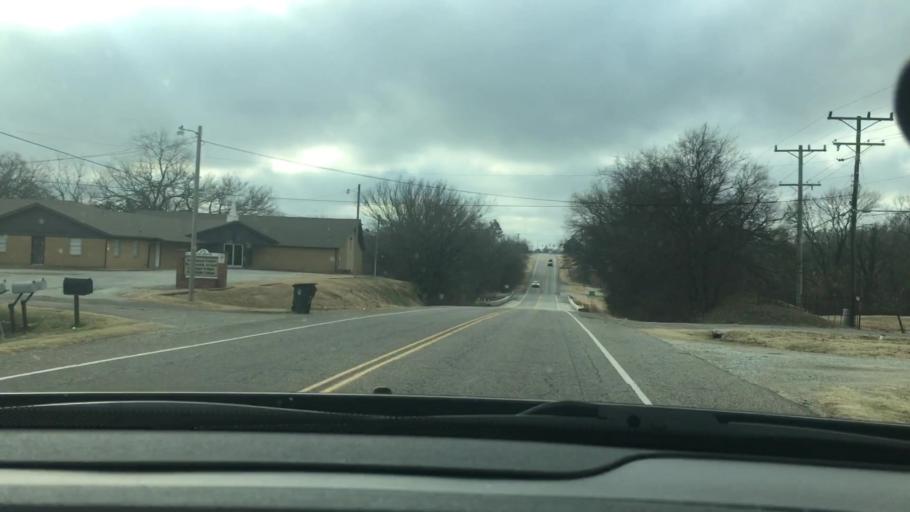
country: US
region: Oklahoma
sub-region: Bryan County
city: Durant
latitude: 34.0125
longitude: -96.3730
